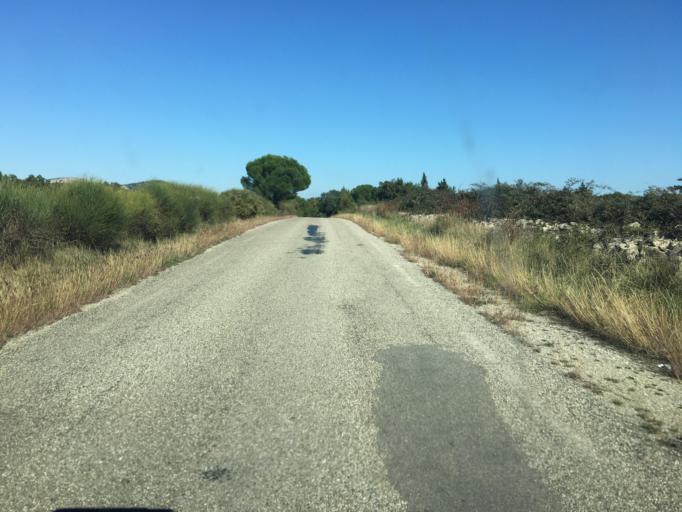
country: FR
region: Languedoc-Roussillon
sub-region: Departement du Gard
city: Barjac
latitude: 44.1708
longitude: 4.3207
